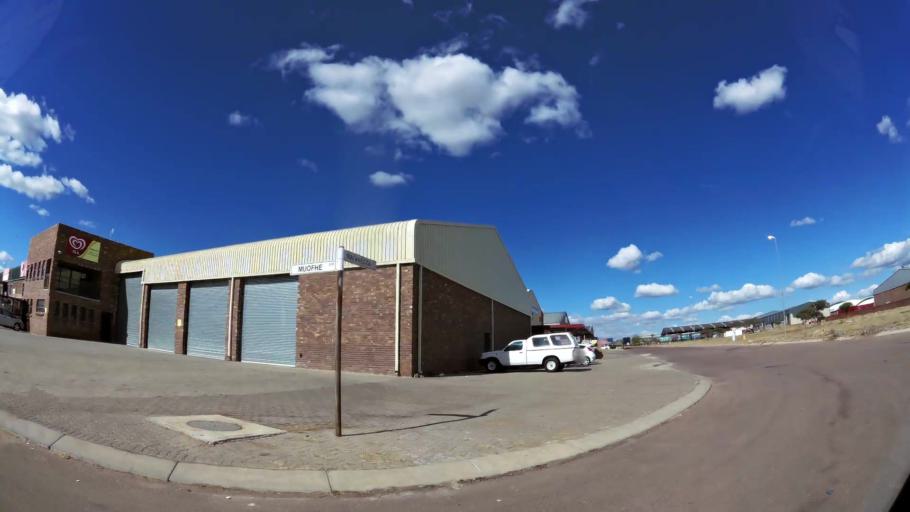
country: ZA
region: Limpopo
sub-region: Capricorn District Municipality
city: Polokwane
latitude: -23.8636
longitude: 29.4777
